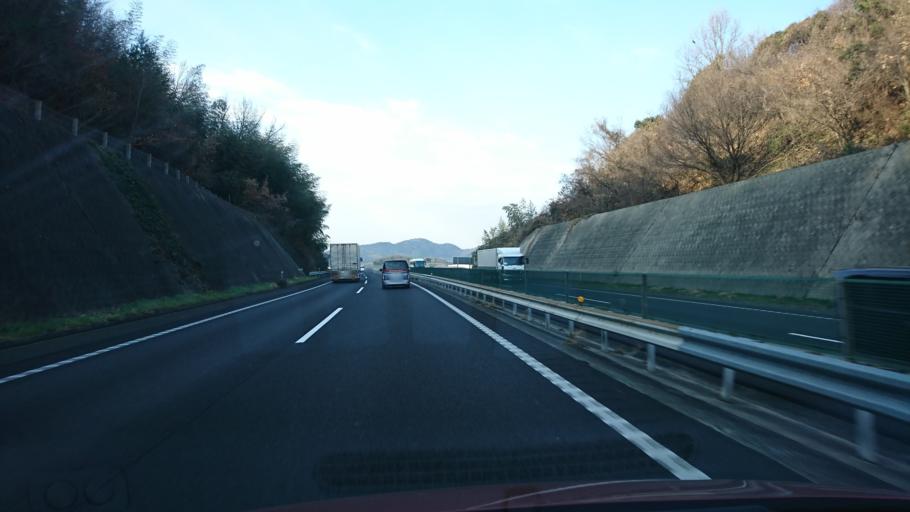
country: JP
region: Hyogo
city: Tatsunocho-tominaga
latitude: 34.8460
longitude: 134.5220
